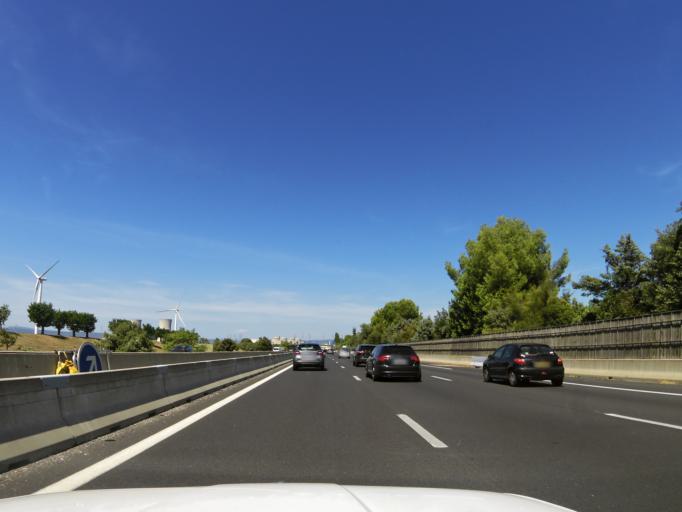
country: FR
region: Provence-Alpes-Cote d'Azur
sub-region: Departement du Vaucluse
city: Bollene
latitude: 44.3114
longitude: 4.7454
